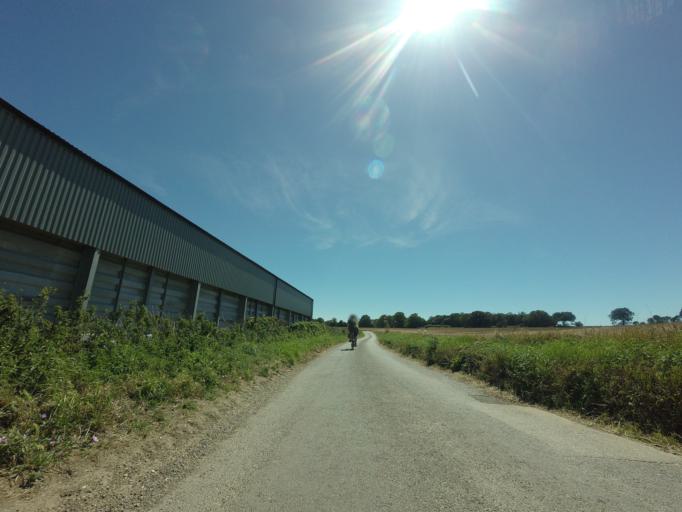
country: GB
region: England
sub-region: Kent
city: Deal
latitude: 51.1952
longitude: 1.3628
